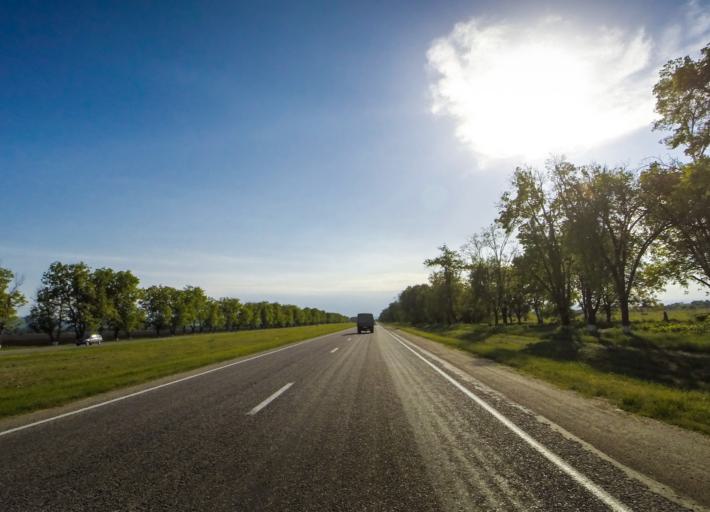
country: RU
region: Kabardino-Balkariya
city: Nartan
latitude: 43.4959
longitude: 43.7009
